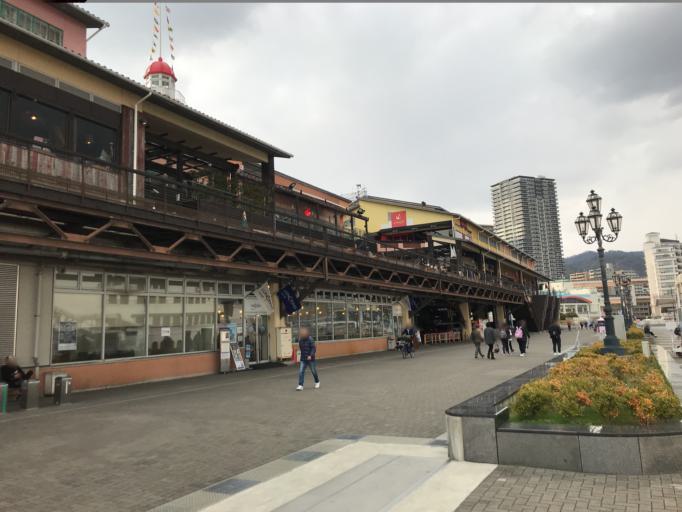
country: JP
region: Hyogo
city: Kobe
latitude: 34.6795
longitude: 135.1852
